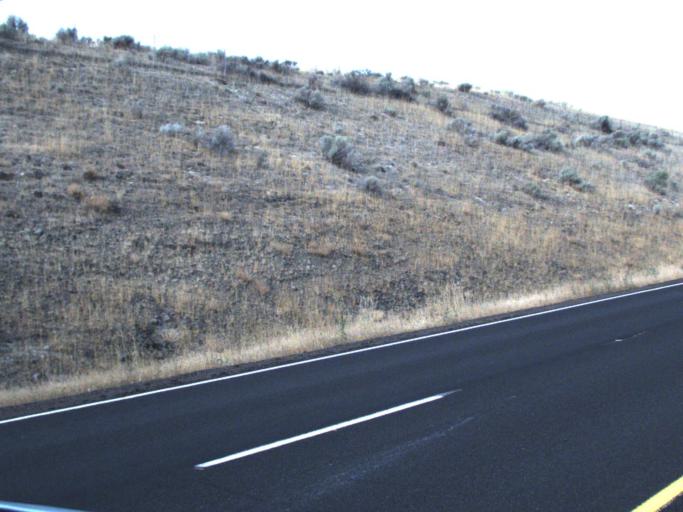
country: US
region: Washington
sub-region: Yakima County
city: Toppenish
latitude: 46.2772
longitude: -120.3793
